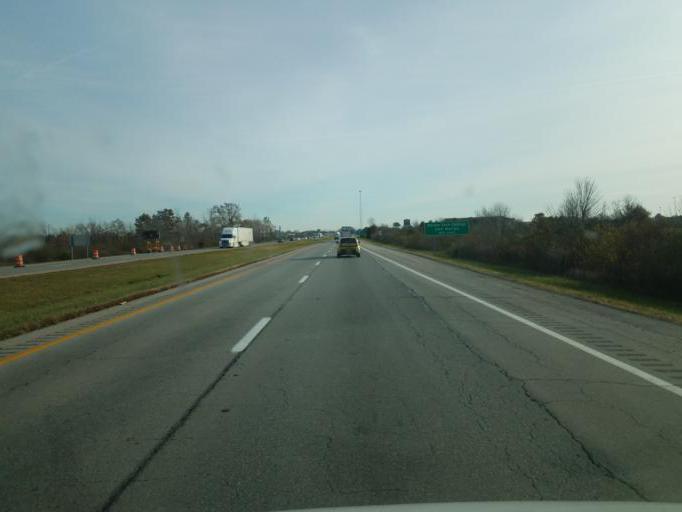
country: US
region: Ohio
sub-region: Marion County
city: Marion
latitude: 40.5891
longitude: -83.0807
